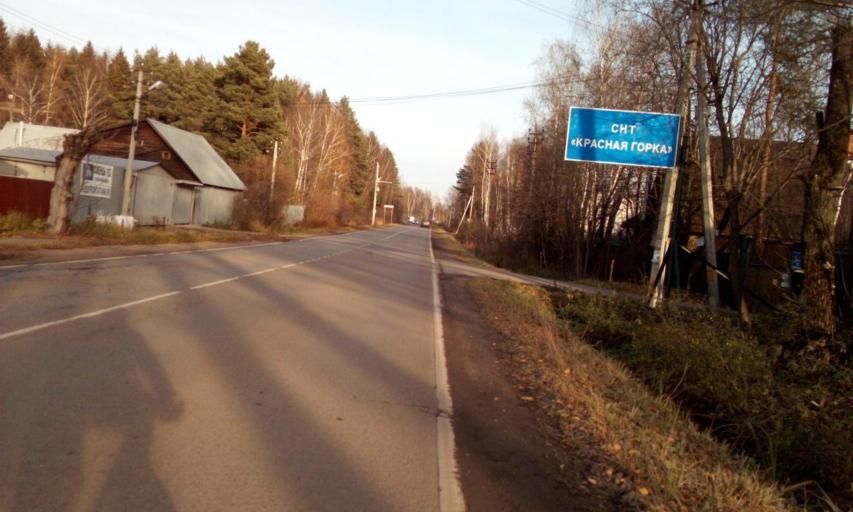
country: RU
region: Moskovskaya
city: Aprelevka
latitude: 55.5706
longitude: 37.1004
